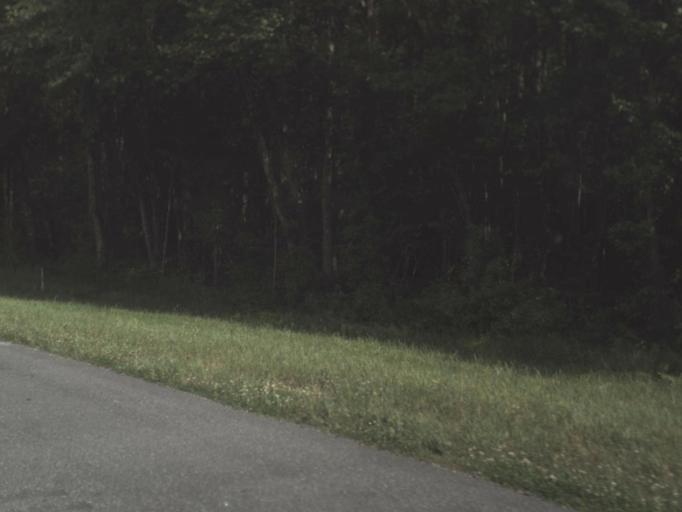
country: US
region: Florida
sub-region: Columbia County
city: Watertown
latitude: 30.2485
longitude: -82.5431
